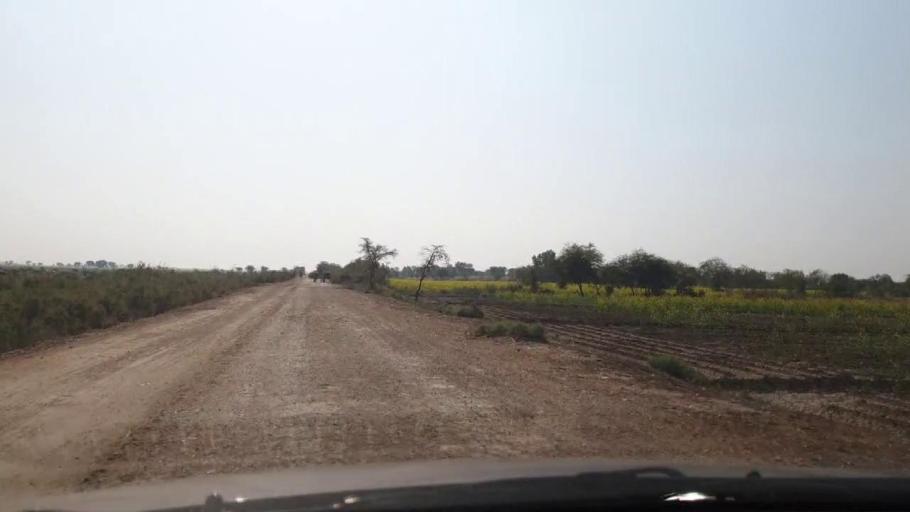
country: PK
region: Sindh
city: Jhol
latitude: 25.8829
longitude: 68.9972
